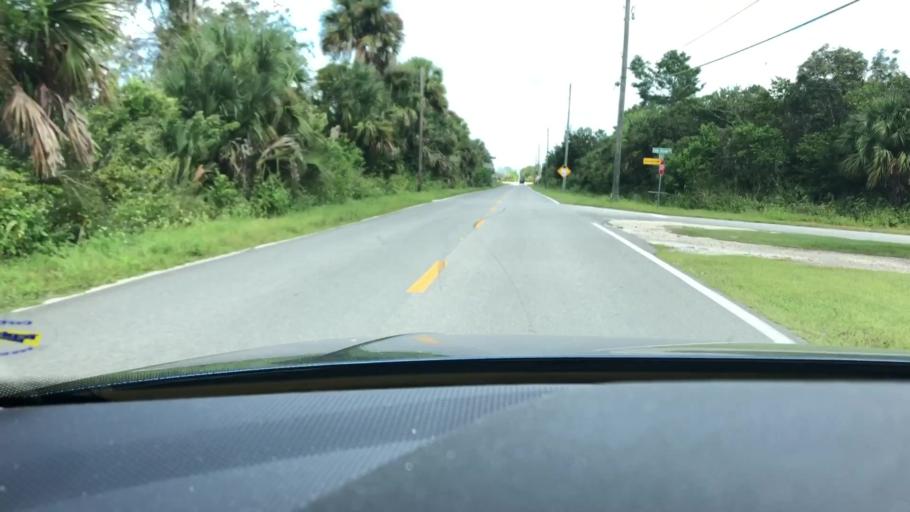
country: US
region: Florida
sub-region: Volusia County
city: Edgewater
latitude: 28.9468
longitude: -80.9438
